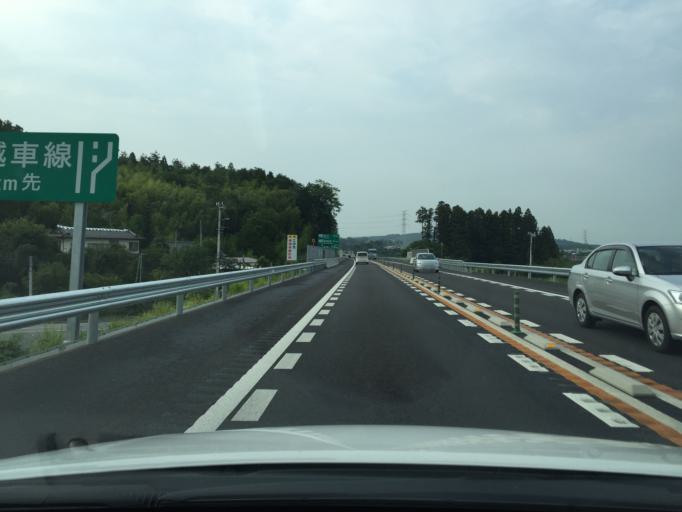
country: JP
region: Fukushima
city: Namie
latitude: 37.3913
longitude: 140.9666
